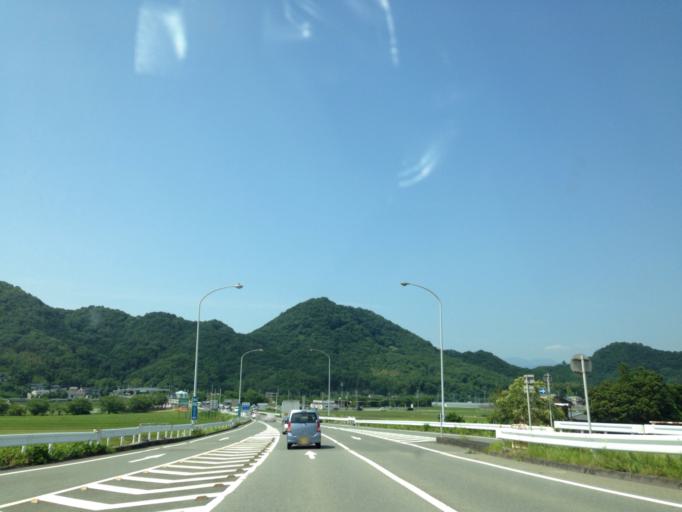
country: JP
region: Shizuoka
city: Mishima
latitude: 35.0531
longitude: 138.9240
